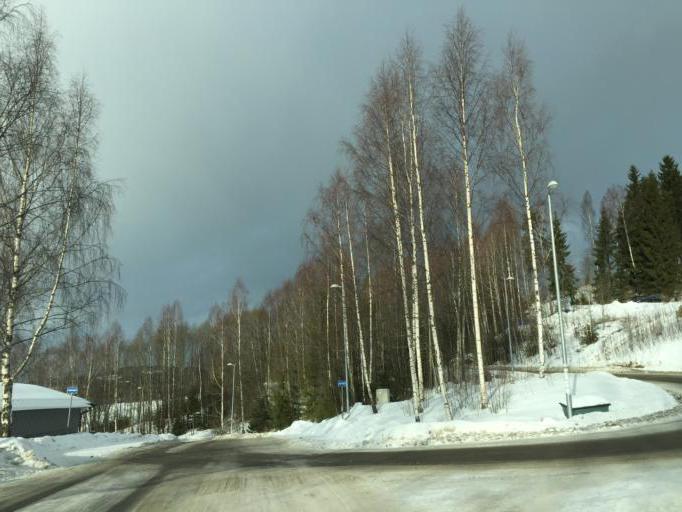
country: NO
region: Hedmark
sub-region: Kongsvinger
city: Kongsvinger
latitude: 60.2076
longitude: 11.9746
